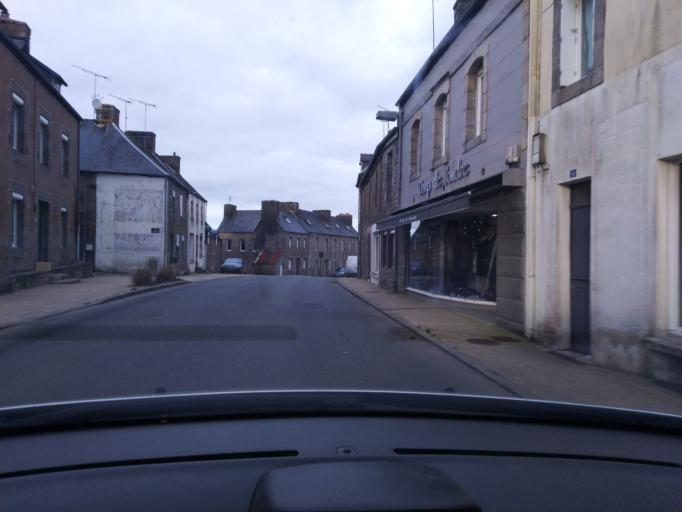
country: FR
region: Brittany
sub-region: Departement des Cotes-d'Armor
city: Plouaret
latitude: 48.6128
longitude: -3.4728
